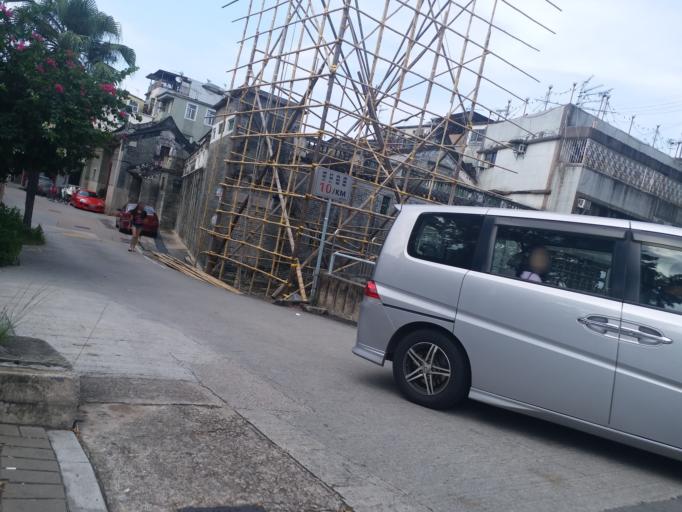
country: HK
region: Yuen Long
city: Yuen Long Kau Hui
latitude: 22.4439
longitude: 114.0072
